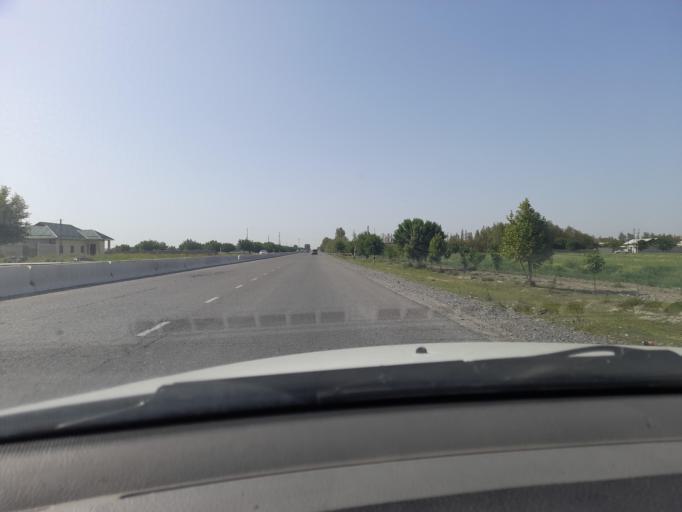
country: UZ
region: Samarqand
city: Daxbet
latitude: 39.8044
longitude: 66.8621
